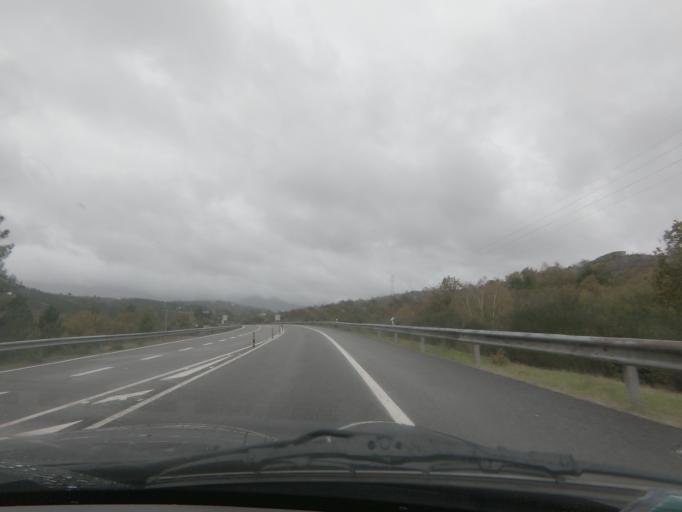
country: PT
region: Vila Real
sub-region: Santa Marta de Penaguiao
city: Santa Marta de Penaguiao
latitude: 41.2846
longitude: -7.8192
